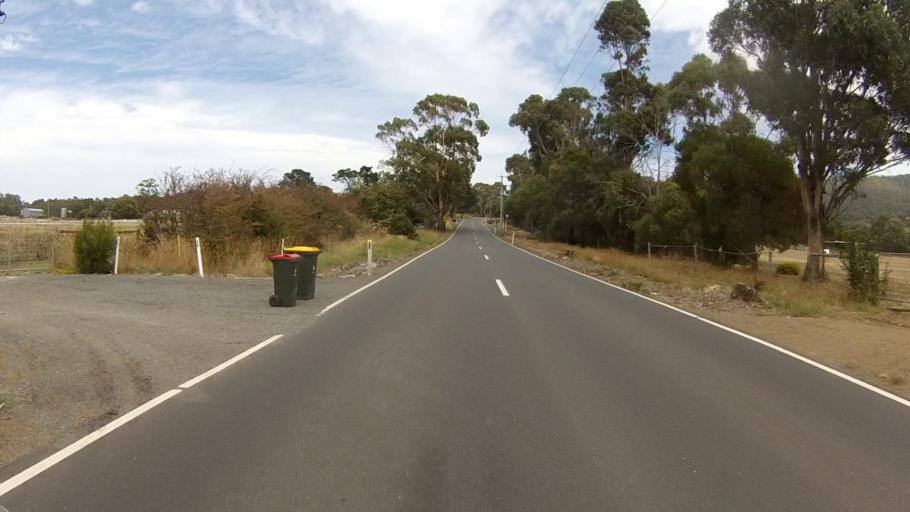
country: AU
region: Tasmania
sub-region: Clarence
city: Acton Park
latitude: -42.8659
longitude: 147.4889
